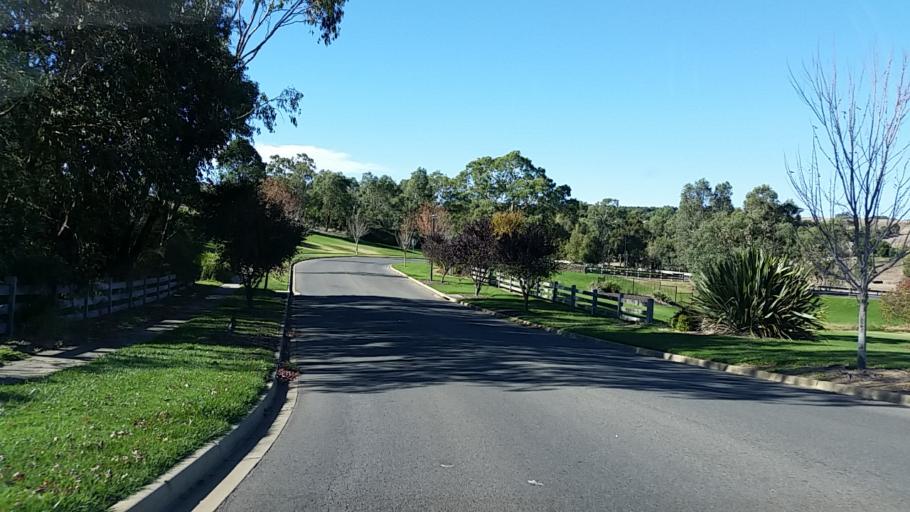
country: AU
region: South Australia
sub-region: Mount Barker
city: Mount Barker
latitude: -35.0657
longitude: 138.8900
